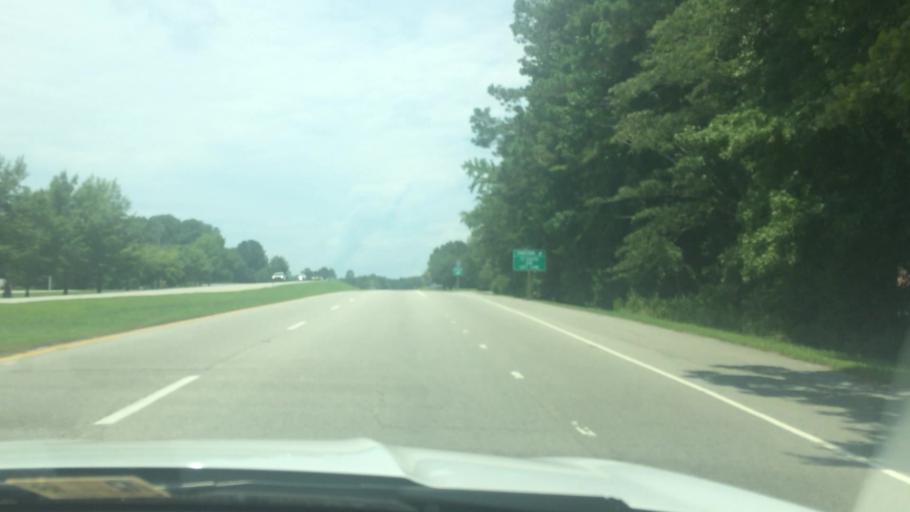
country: US
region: Virginia
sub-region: York County
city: Yorktown
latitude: 37.1698
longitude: -76.5636
